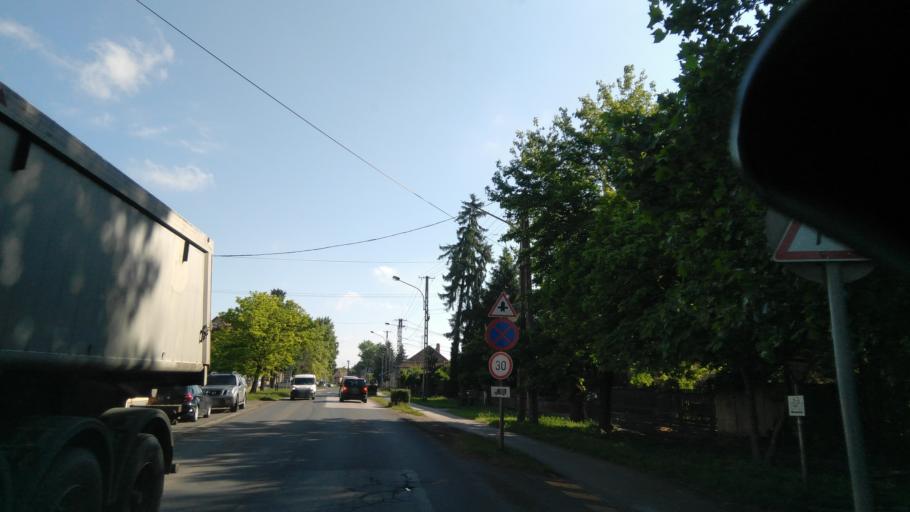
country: HU
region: Bekes
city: Bekes
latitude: 46.7741
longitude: 21.1349
